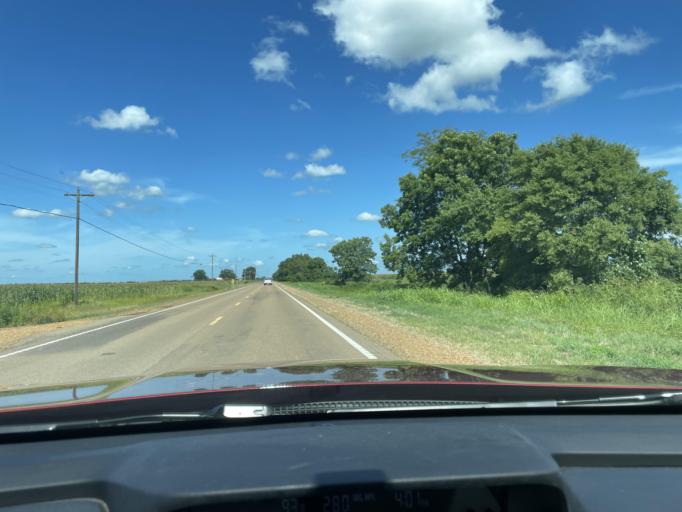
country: US
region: Mississippi
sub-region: Humphreys County
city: Belzoni
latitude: 33.1837
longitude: -90.5314
